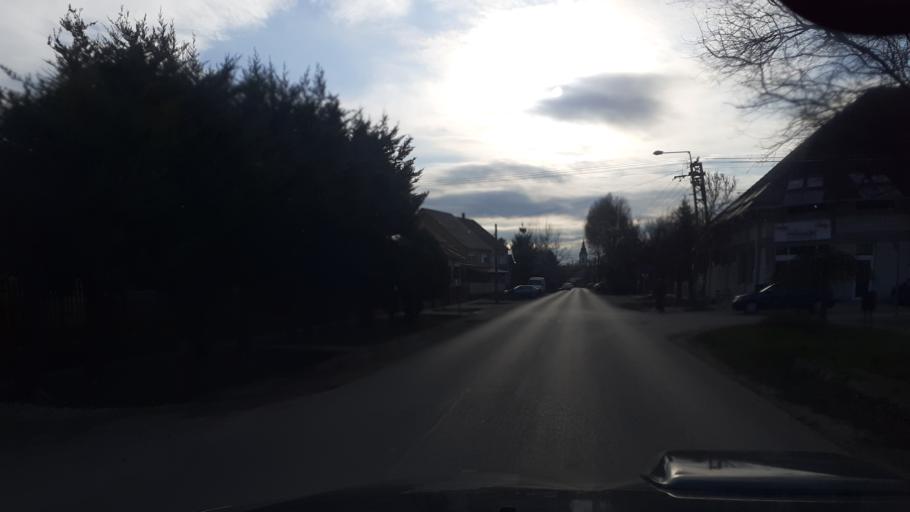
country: HU
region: Bacs-Kiskun
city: Kunszentmiklos
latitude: 47.0324
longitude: 19.1277
